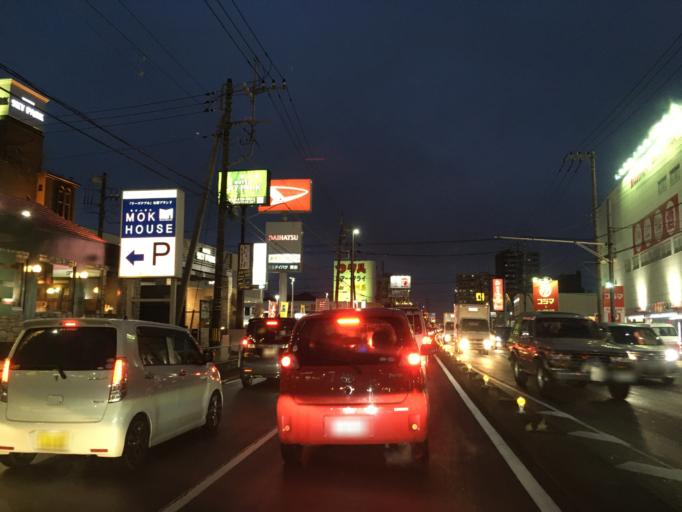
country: JP
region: Saitama
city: Shiki
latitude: 35.7998
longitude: 139.5613
